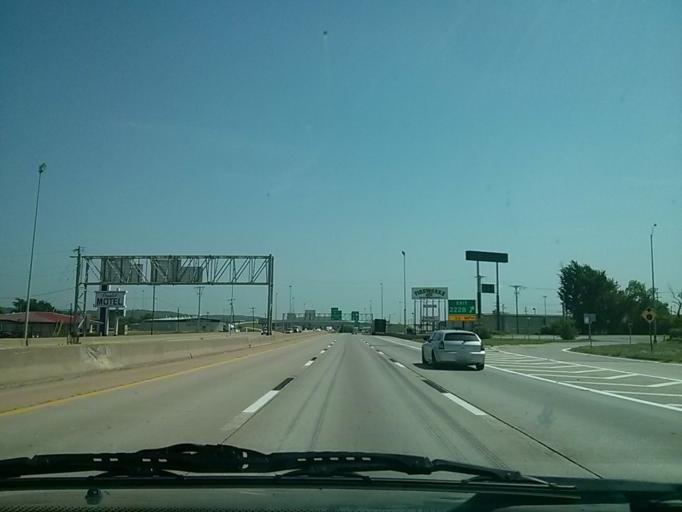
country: US
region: Oklahoma
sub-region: Tulsa County
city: Oakhurst
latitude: 36.0831
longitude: -96.0450
